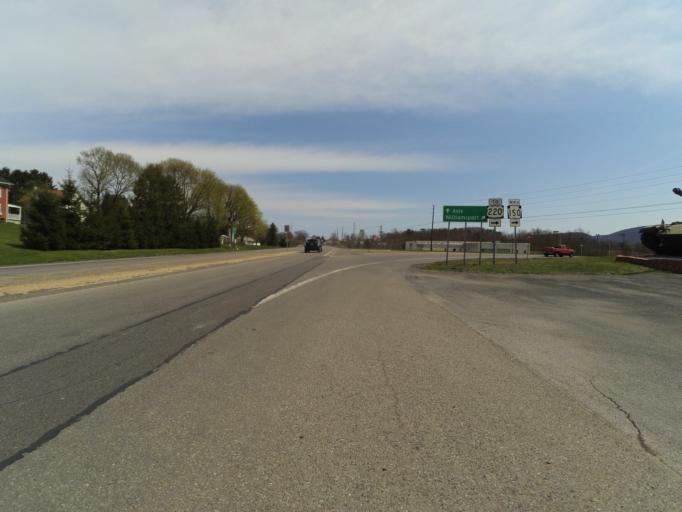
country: US
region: Pennsylvania
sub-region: Clinton County
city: Avis
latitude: 41.1808
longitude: -77.3279
